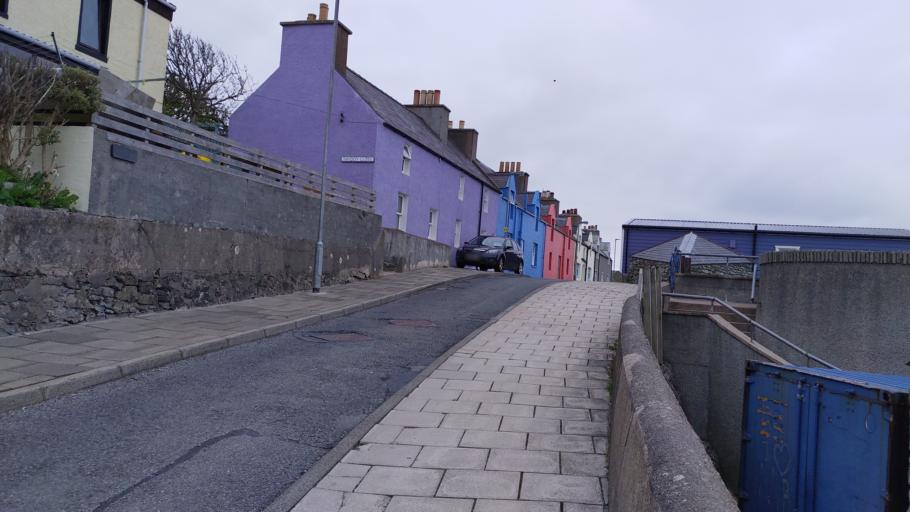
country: GB
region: Scotland
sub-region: Shetland Islands
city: Lerwick
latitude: 60.1368
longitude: -1.2752
